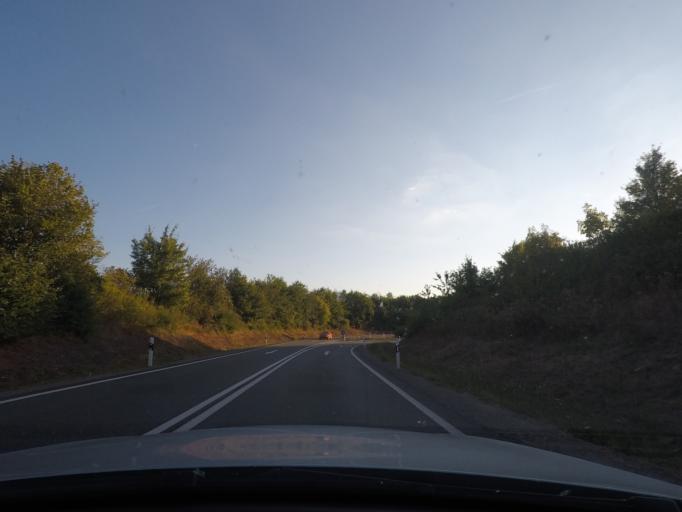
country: DE
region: Rheinland-Pfalz
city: Dreisen
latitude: 49.6070
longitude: 8.0050
